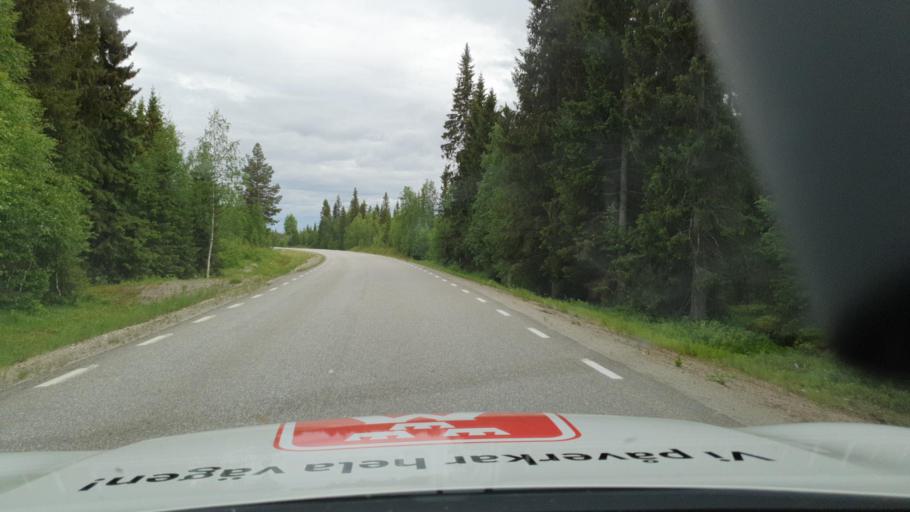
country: SE
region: Vaesterbotten
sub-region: Lycksele Kommun
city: Soderfors
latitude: 64.3317
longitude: 18.1436
